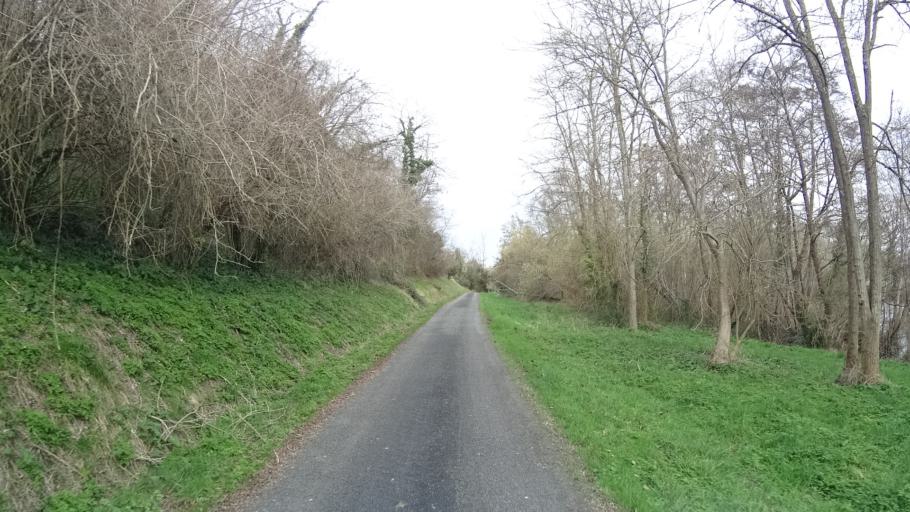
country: FR
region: Aquitaine
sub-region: Departement de la Dordogne
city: Saint-Aulaye
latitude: 45.2457
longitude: 0.1507
